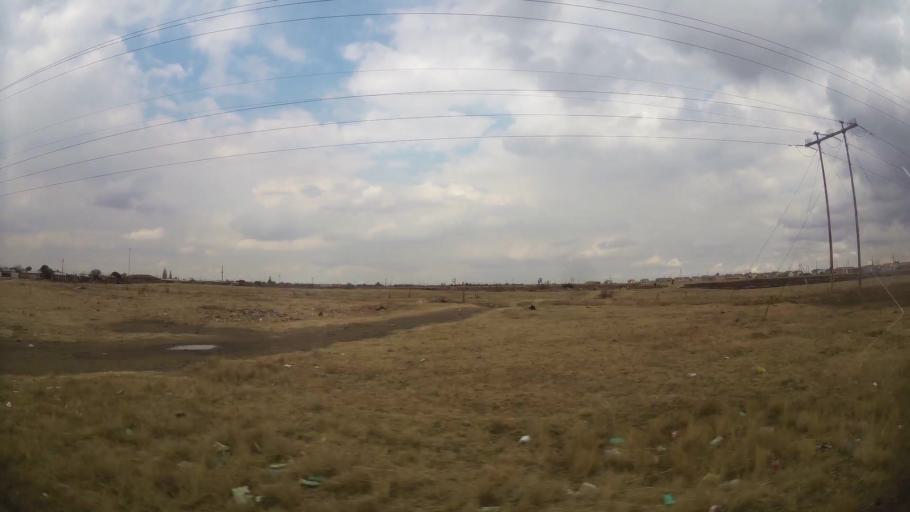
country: ZA
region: Orange Free State
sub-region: Fezile Dabi District Municipality
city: Sasolburg
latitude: -26.8551
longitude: 27.8669
